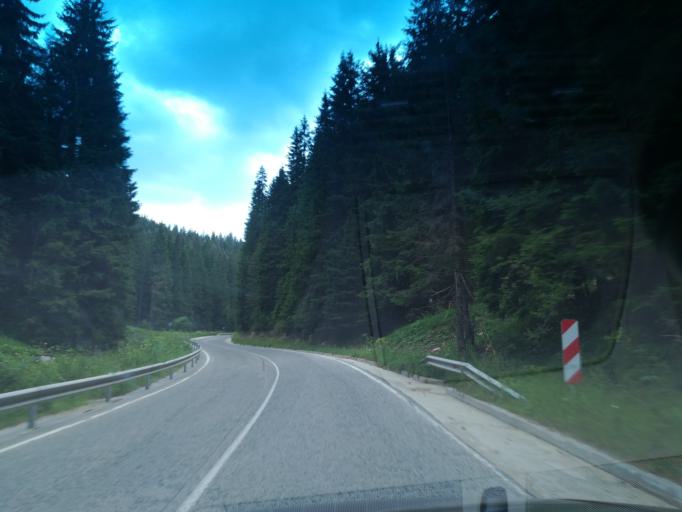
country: BG
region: Smolyan
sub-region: Obshtina Chepelare
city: Chepelare
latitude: 41.6669
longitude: 24.7141
